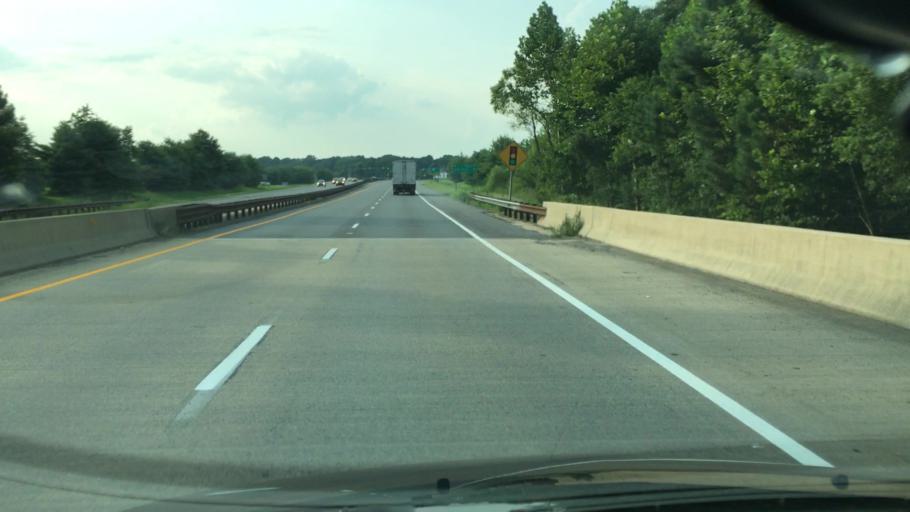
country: US
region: Maryland
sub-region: Worcester County
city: Ocean Pines
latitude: 38.4012
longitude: -75.2093
